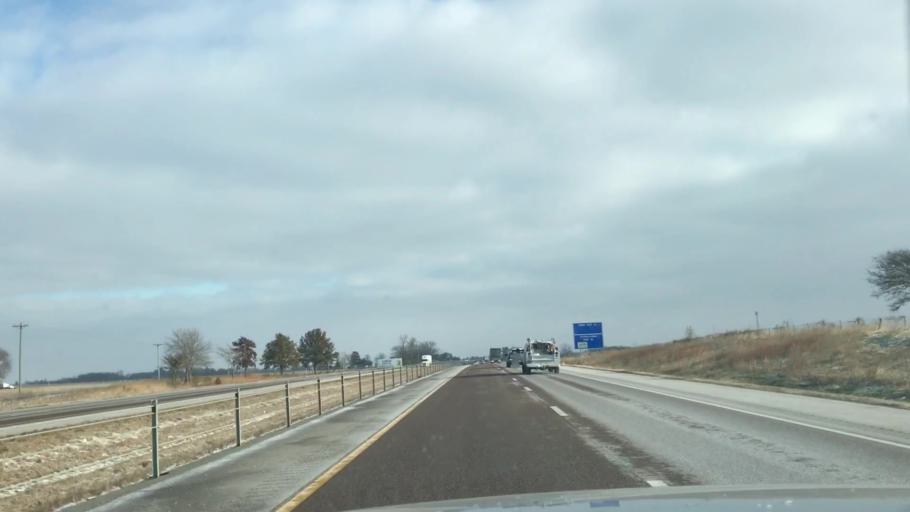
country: US
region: Illinois
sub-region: Madison County
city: Worden
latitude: 38.9139
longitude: -89.8184
